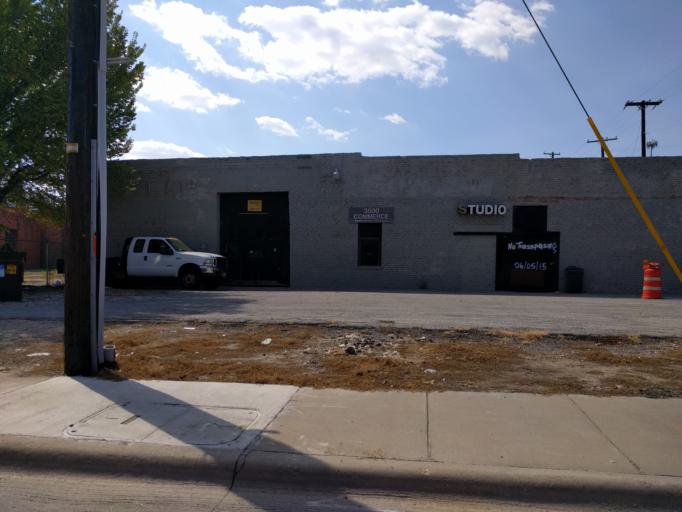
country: US
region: Texas
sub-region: Dallas County
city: Dallas
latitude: 32.7855
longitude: -96.7735
